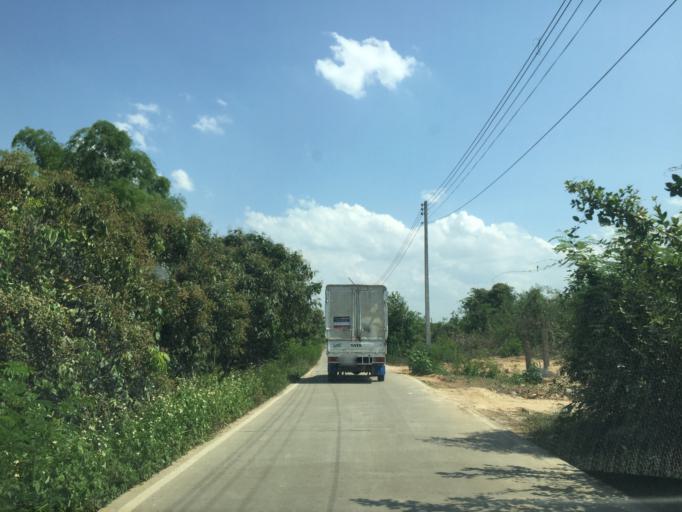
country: TH
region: Lamphun
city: Ban Thi
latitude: 18.6388
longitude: 99.0542
